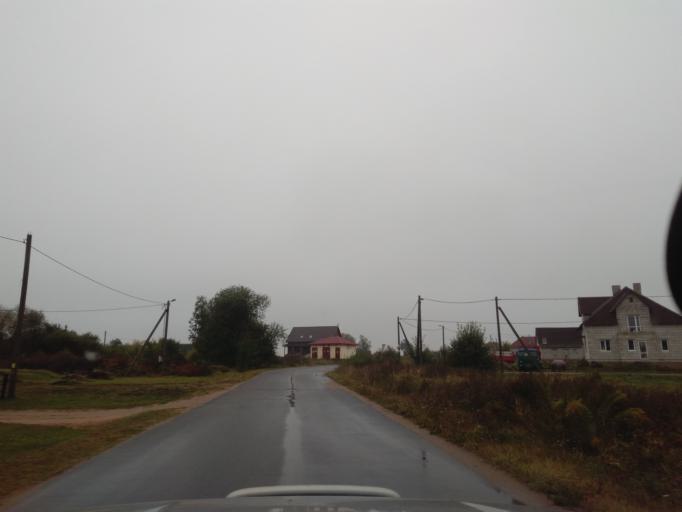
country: BY
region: Minsk
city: Kapyl'
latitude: 53.1598
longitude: 27.1000
